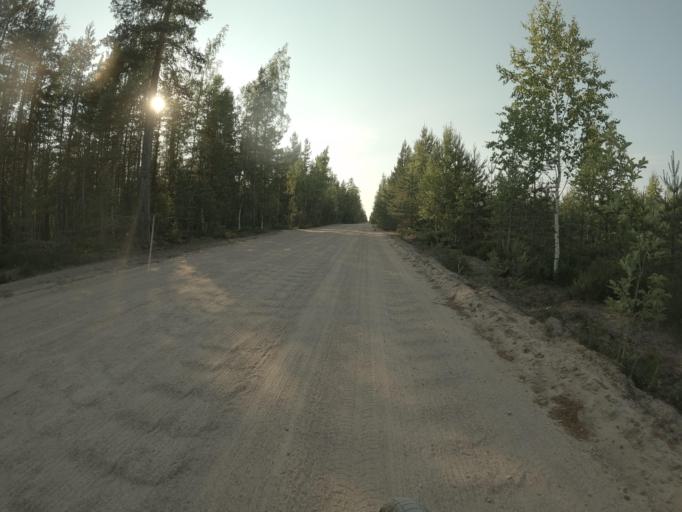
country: RU
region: Leningrad
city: Yakovlevo
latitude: 60.4545
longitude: 29.2529
